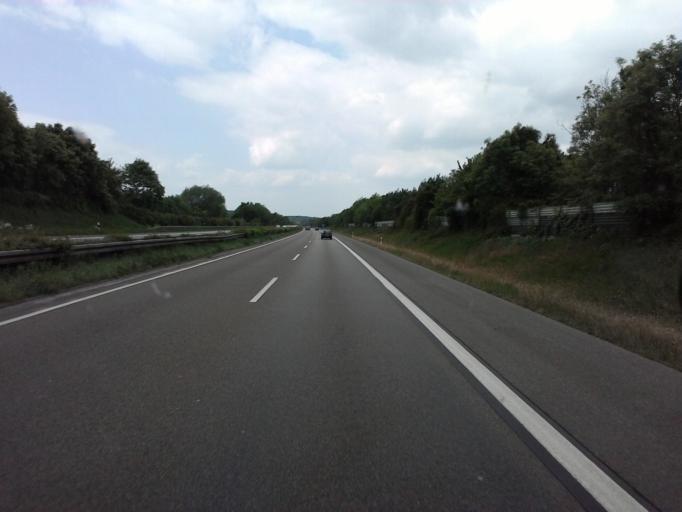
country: DE
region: North Rhine-Westphalia
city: Rheinberg
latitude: 51.5512
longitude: 6.5500
